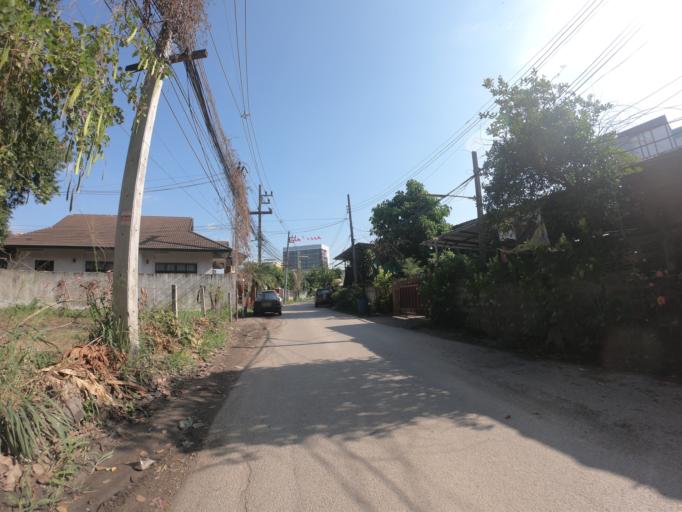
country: TH
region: Chiang Mai
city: Chiang Mai
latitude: 18.7949
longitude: 99.0197
